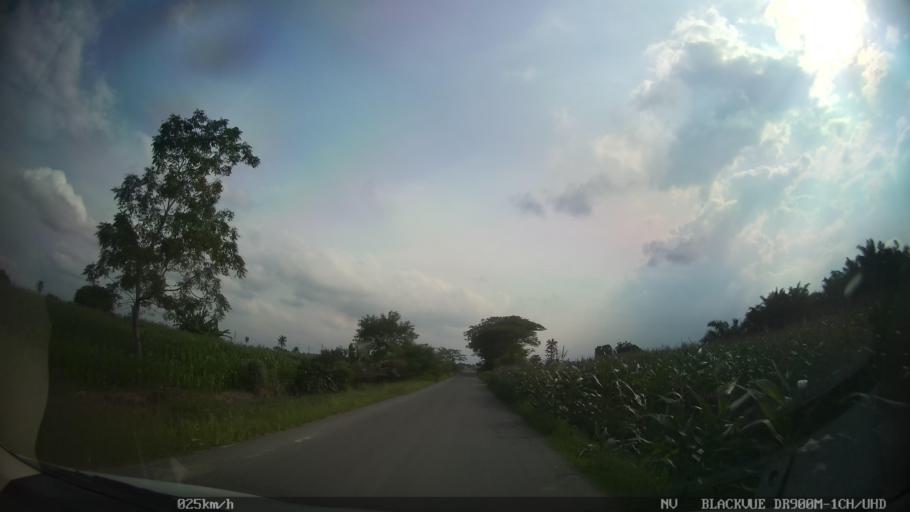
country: ID
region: North Sumatra
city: Percut
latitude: 3.5721
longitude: 98.7777
